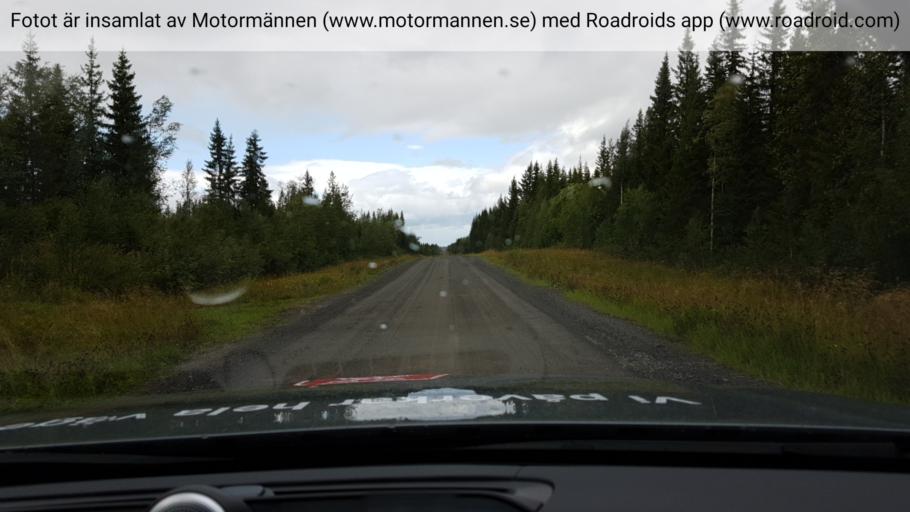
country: SE
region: Jaemtland
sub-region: OEstersunds Kommun
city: Lit
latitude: 63.6626
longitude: 14.9080
